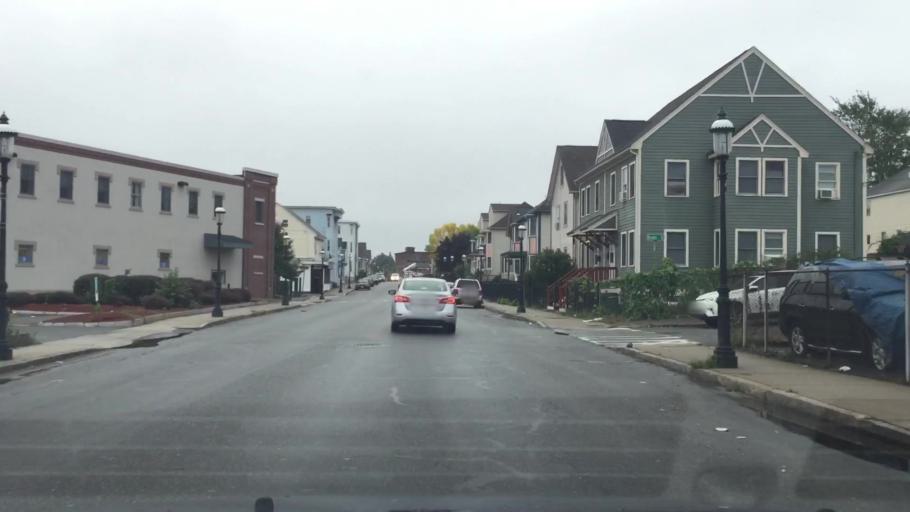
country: US
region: Massachusetts
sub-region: Middlesex County
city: Lowell
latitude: 42.6447
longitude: -71.3212
